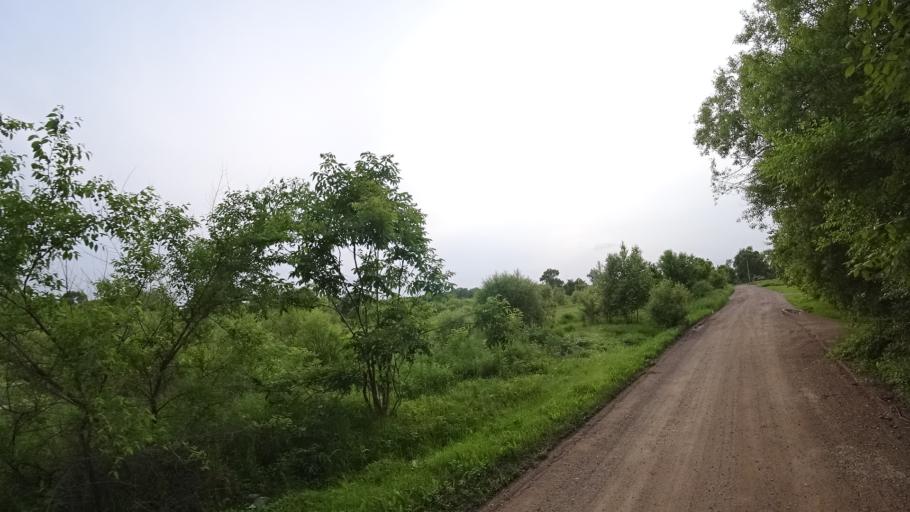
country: RU
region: Primorskiy
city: Novosysoyevka
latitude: 44.2433
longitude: 133.3619
